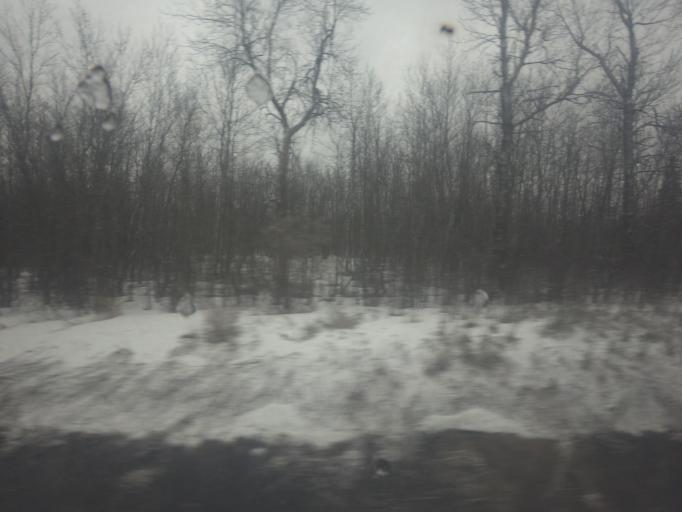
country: CA
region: Ontario
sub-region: Lanark County
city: Smiths Falls
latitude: 44.9368
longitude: -76.0250
